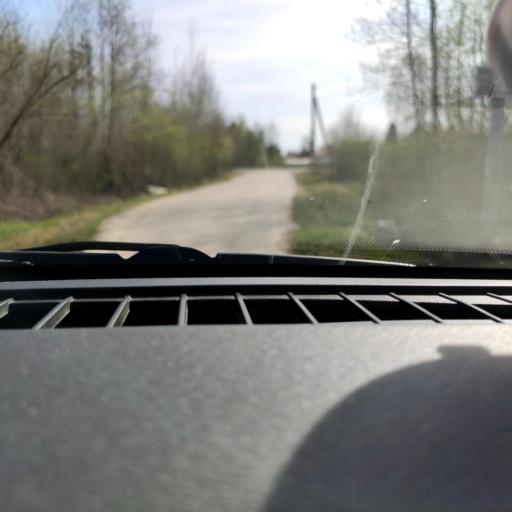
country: RU
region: Perm
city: Kondratovo
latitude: 58.2569
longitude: 56.0994
